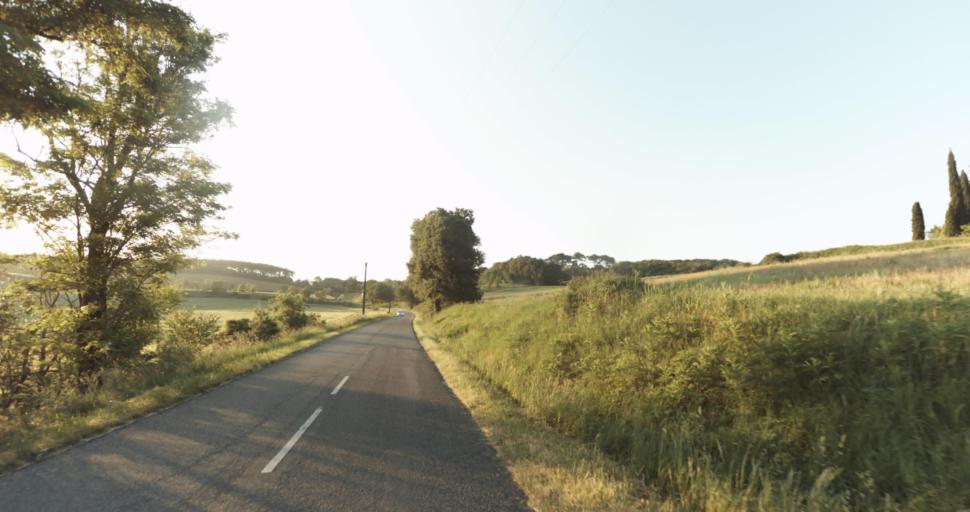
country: FR
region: Midi-Pyrenees
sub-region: Departement du Gers
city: Pujaudran
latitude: 43.6239
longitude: 1.1658
